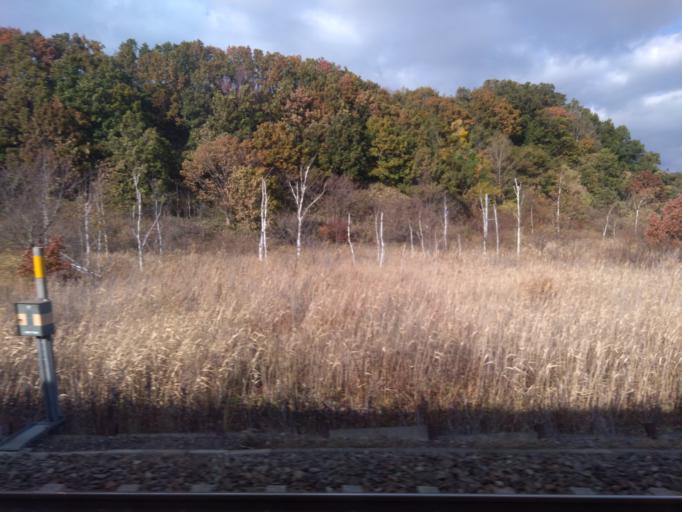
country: JP
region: Hokkaido
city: Date
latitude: 42.4901
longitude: 140.8141
